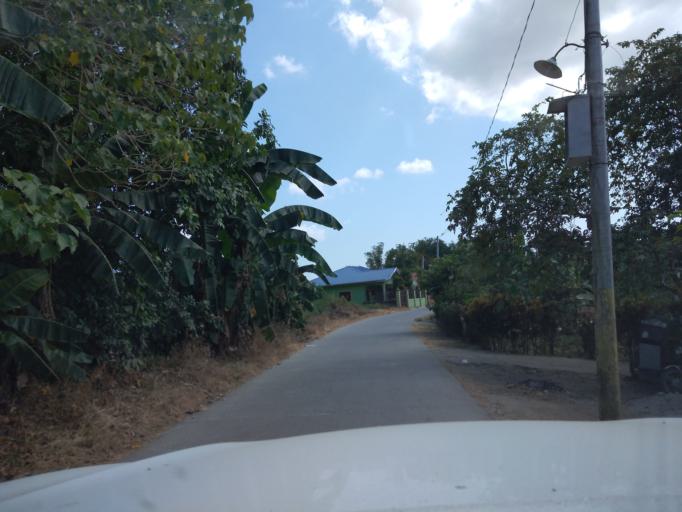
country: PH
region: Central Luzon
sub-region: Province of Pampanga
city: Candaba
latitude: 15.0908
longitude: 120.8149
